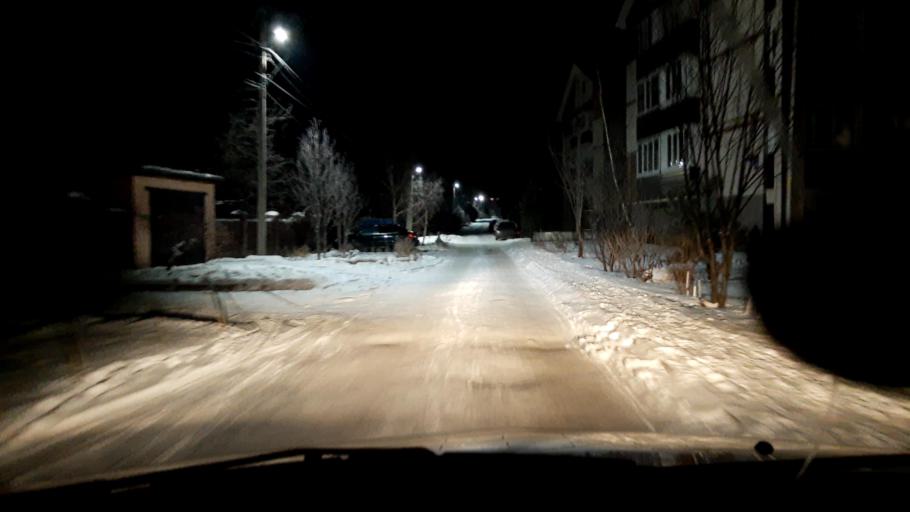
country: RU
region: Bashkortostan
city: Ufa
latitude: 54.6232
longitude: 55.9185
